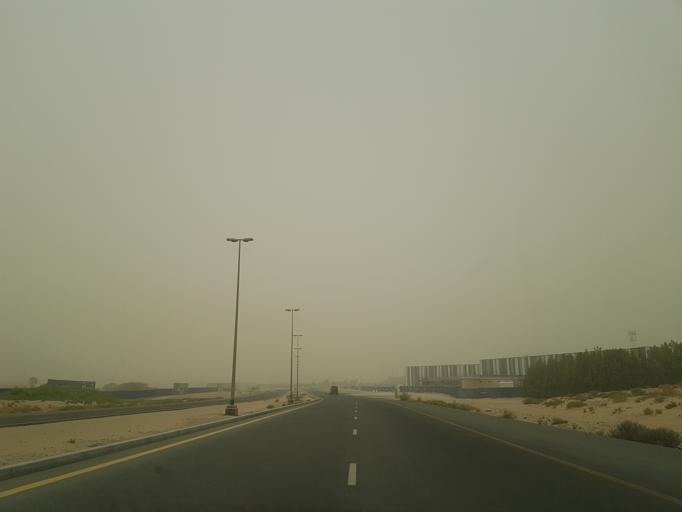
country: AE
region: Dubai
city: Dubai
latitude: 25.1454
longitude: 55.2875
